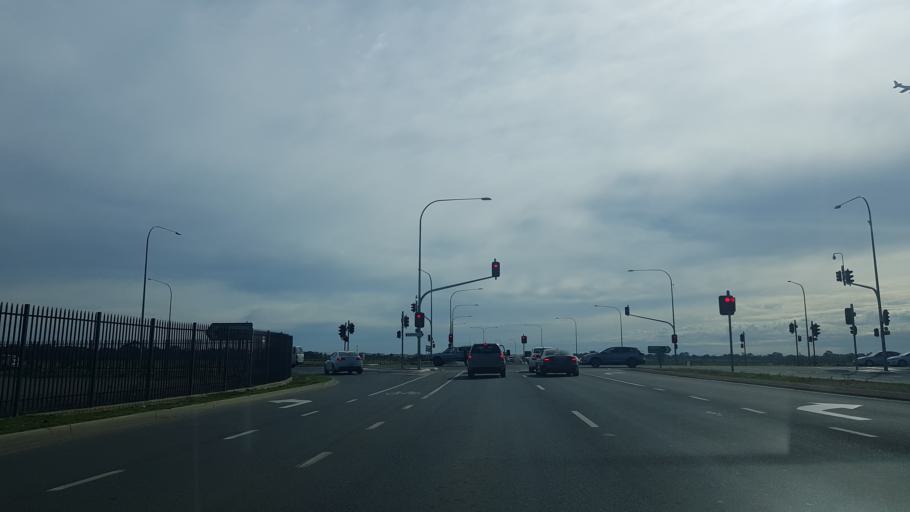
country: AU
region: South Australia
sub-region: Salisbury
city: Ingle Farm
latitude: -34.8096
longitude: 138.6321
